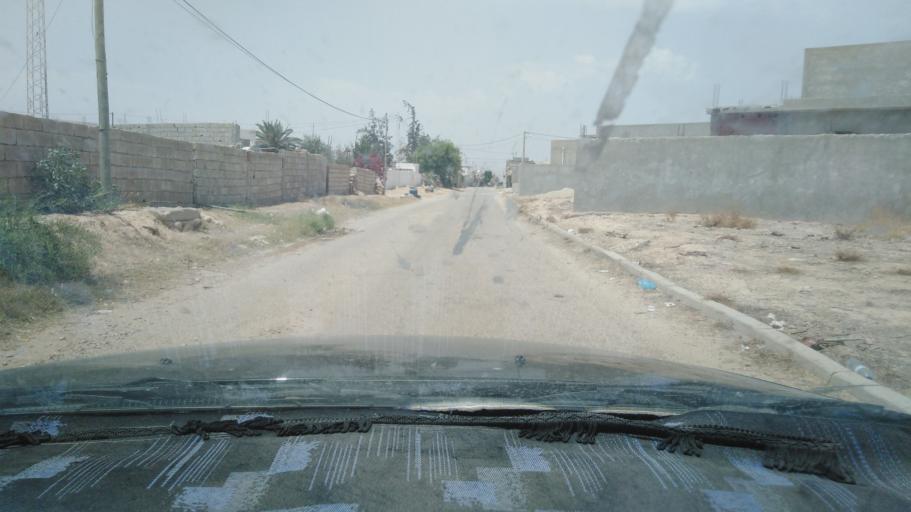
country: TN
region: Qabis
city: Matmata
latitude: 33.6170
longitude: 10.2743
